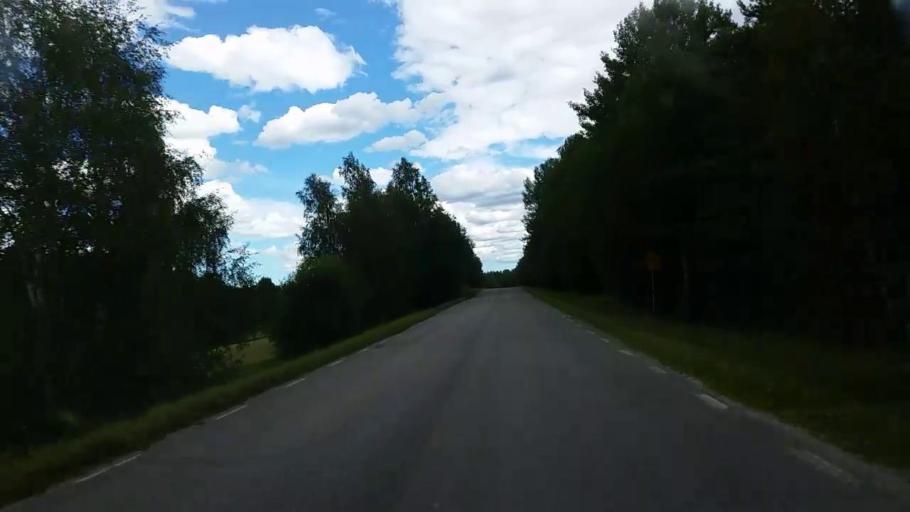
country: SE
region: Gaevleborg
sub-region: Ljusdals Kommun
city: Jaervsoe
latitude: 61.6717
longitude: 16.1217
